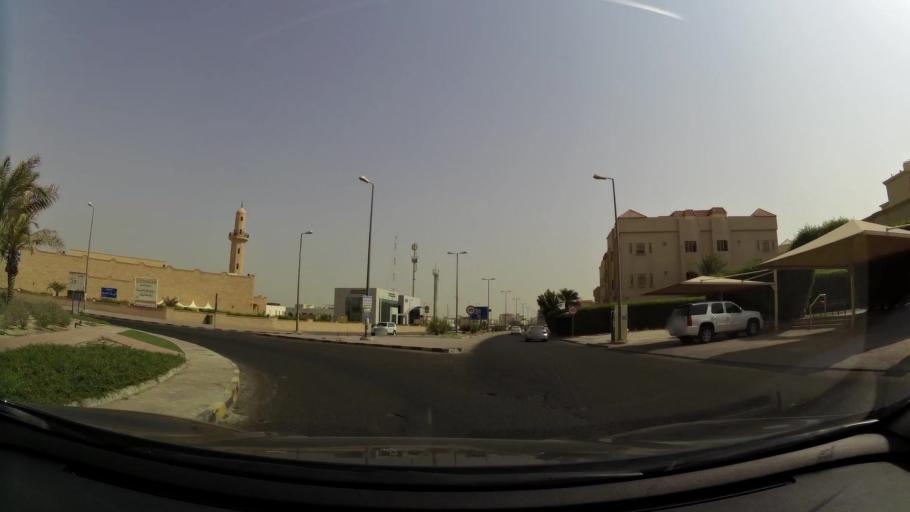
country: KW
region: Muhafazat al Jahra'
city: Al Jahra'
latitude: 29.3065
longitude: 47.7115
